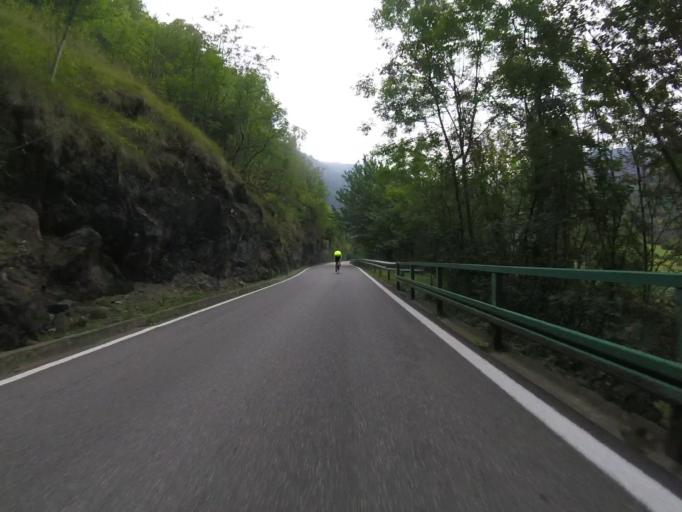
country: IT
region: Lombardy
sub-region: Provincia di Brescia
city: Monno
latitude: 46.2102
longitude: 10.3488
